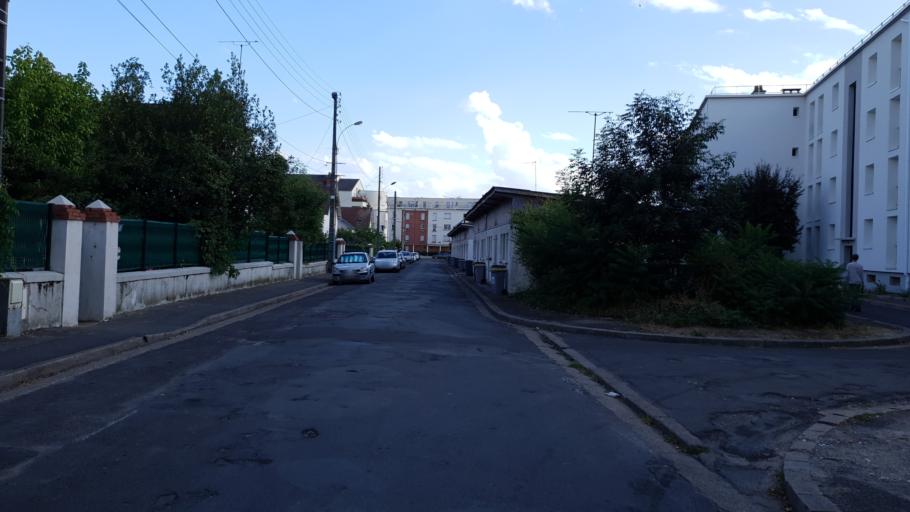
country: FR
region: Centre
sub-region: Departement d'Indre-et-Loire
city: La Riche
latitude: 47.3811
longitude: 0.6731
